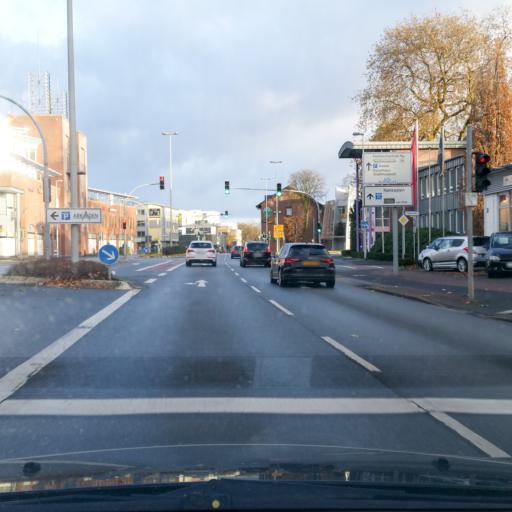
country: DE
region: North Rhine-Westphalia
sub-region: Regierungsbezirk Dusseldorf
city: Bocholt
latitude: 51.8348
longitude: 6.6139
